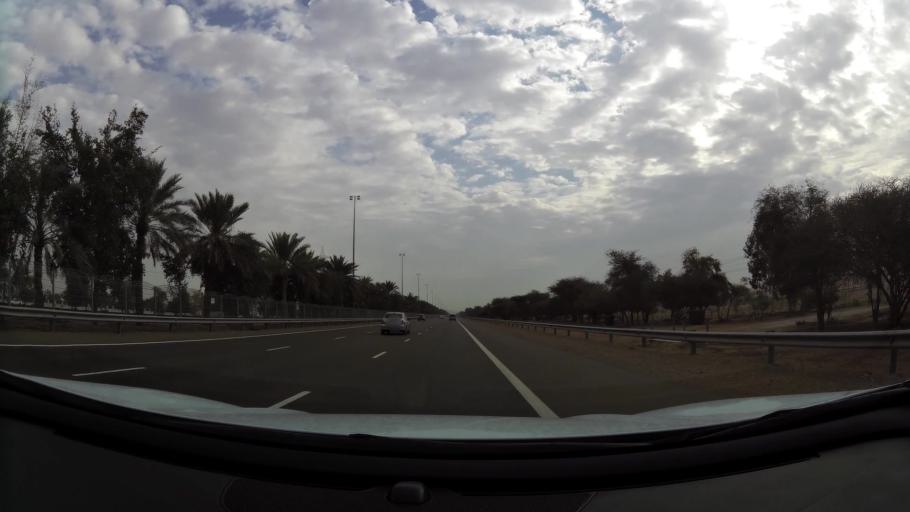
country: AE
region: Abu Dhabi
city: Al Ain
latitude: 24.2170
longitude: 55.5366
